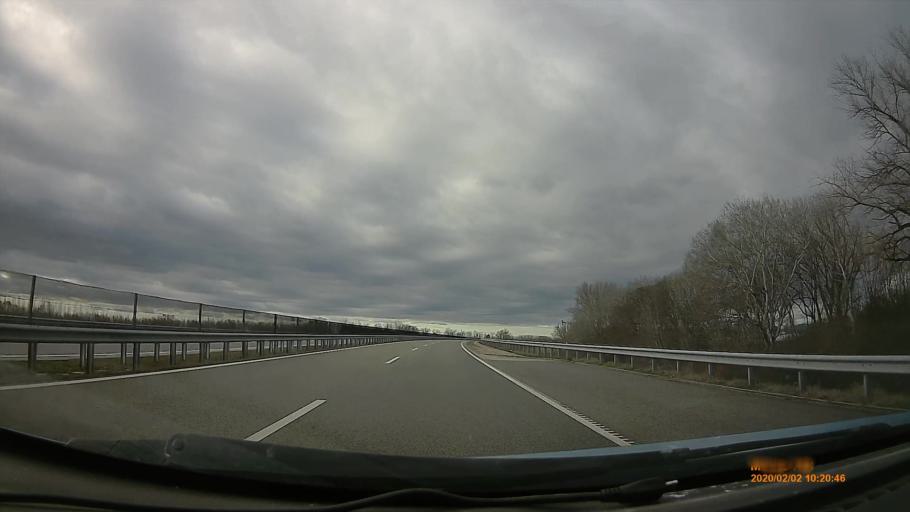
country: HU
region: Gyor-Moson-Sopron
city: Abda
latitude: 47.6649
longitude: 17.5153
